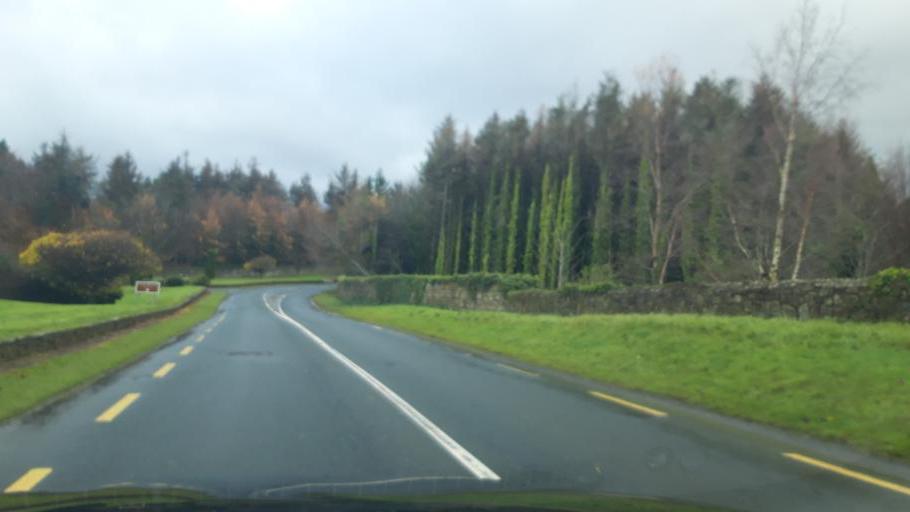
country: IE
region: Leinster
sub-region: Wicklow
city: Kilcoole
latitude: 53.1001
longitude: -6.0745
